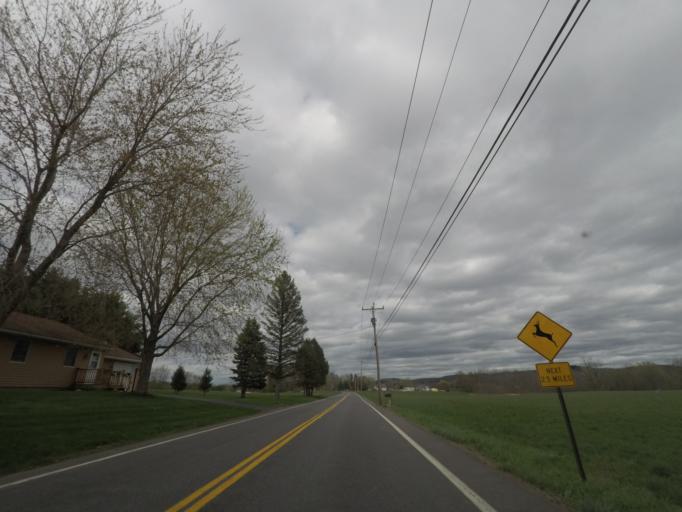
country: US
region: New York
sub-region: Columbia County
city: Philmont
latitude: 42.2846
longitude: -73.6527
